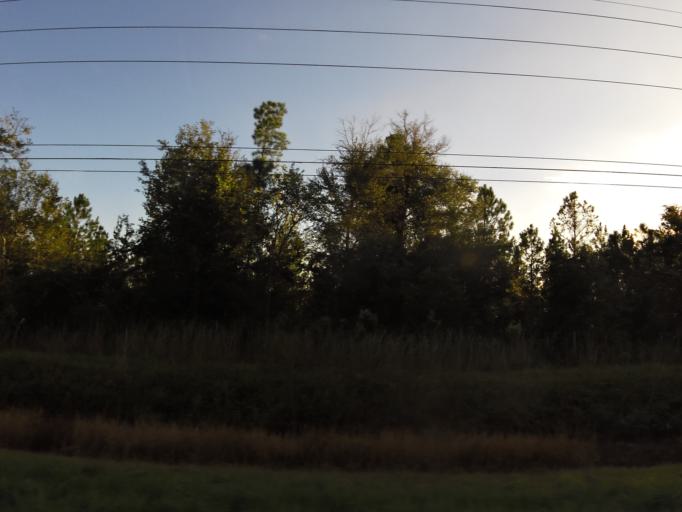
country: US
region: Florida
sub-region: Saint Johns County
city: Fruit Cove
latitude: 30.0604
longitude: -81.6404
